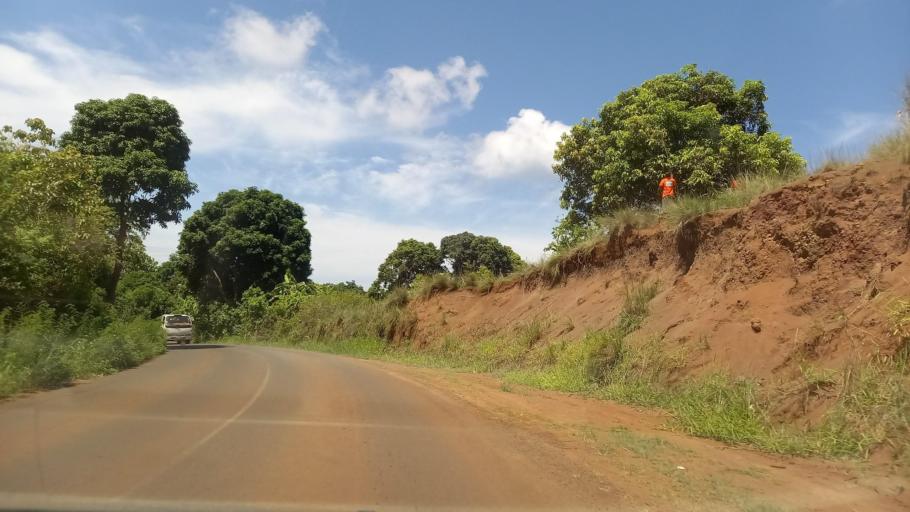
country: YT
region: M'Tsangamouji
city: M'Tsangamouji
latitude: -12.7516
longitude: 45.0911
